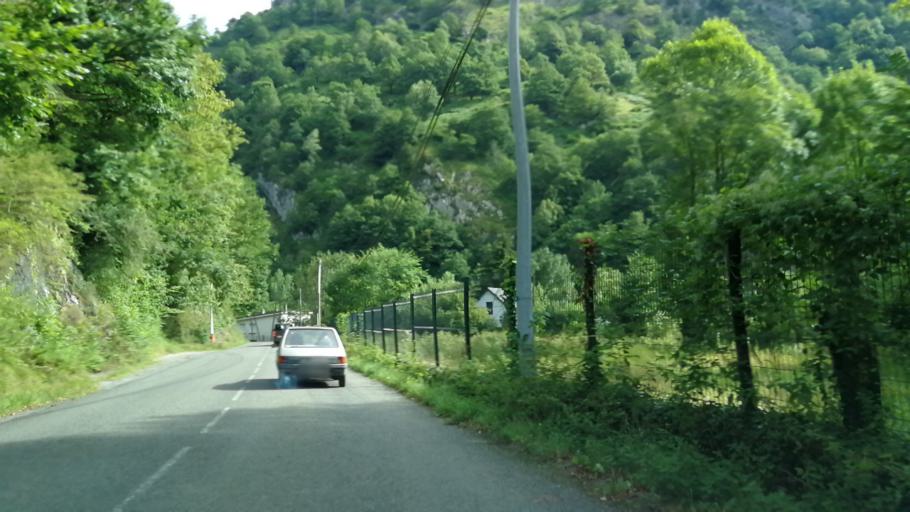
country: FR
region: Aquitaine
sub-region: Departement des Pyrenees-Atlantiques
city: Arette
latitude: 42.9443
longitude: -0.6116
